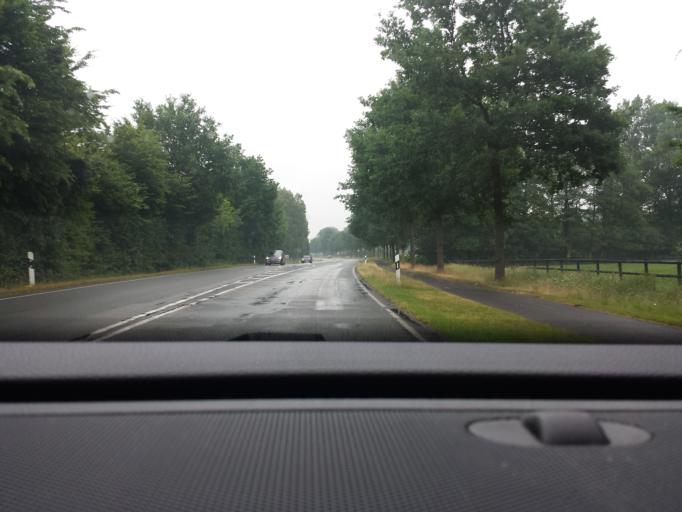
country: DE
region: North Rhine-Westphalia
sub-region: Regierungsbezirk Munster
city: Gronau
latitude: 52.2083
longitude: 6.9803
